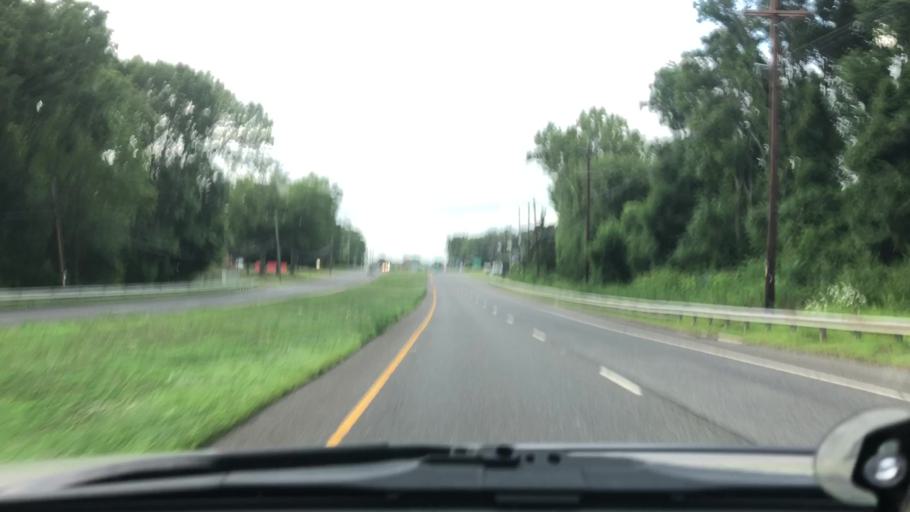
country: US
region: New Jersey
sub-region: Burlington County
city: Bordentown
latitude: 40.1319
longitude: -74.7047
